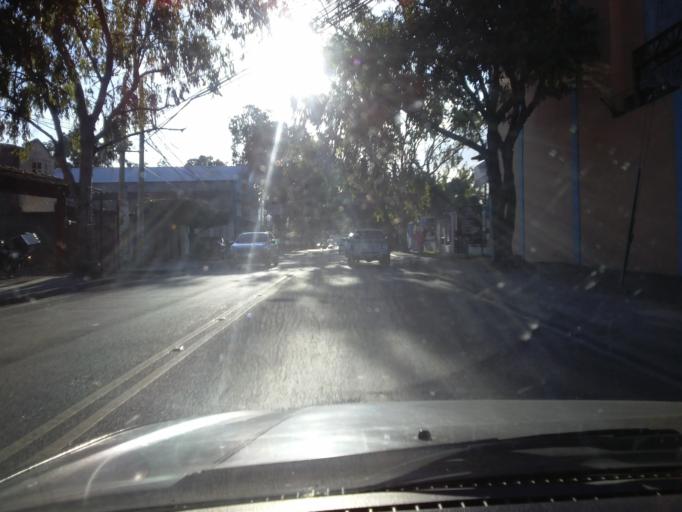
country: HN
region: Francisco Morazan
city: Tegucigalpa
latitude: 14.0533
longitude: -87.2274
